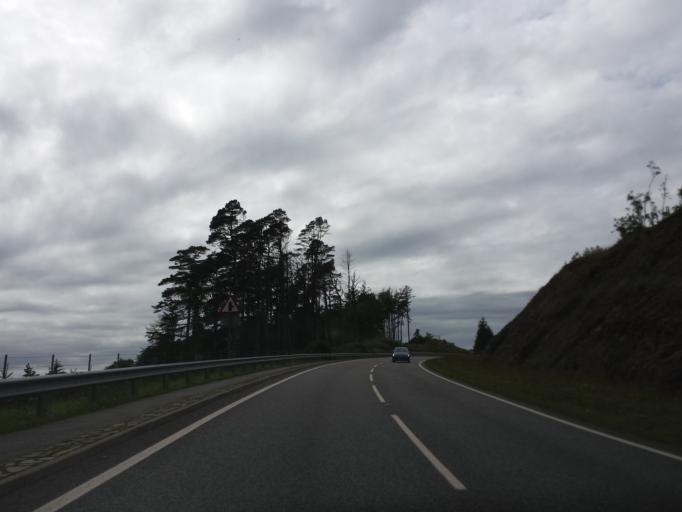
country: GB
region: Scotland
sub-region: Argyll and Bute
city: Isle Of Mull
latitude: 56.8991
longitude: -5.7921
